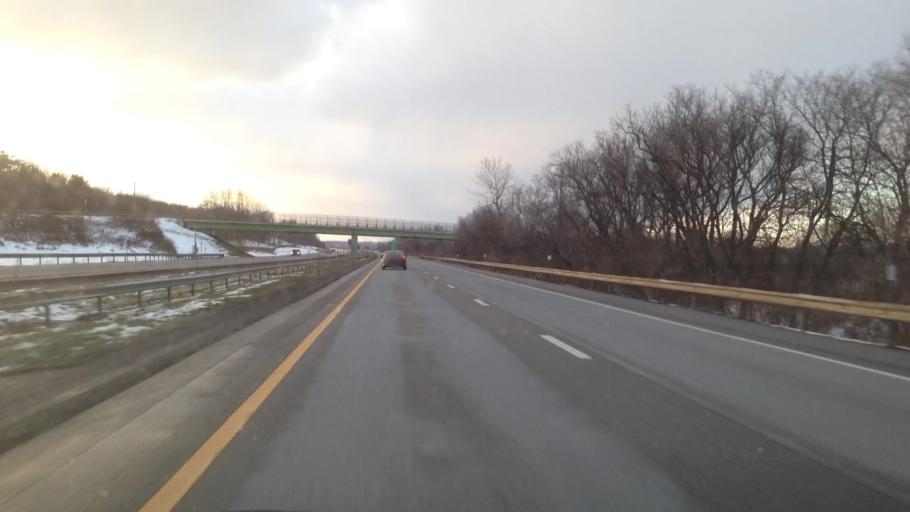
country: US
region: New York
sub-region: Herkimer County
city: Herkimer
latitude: 43.0145
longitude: -74.9448
